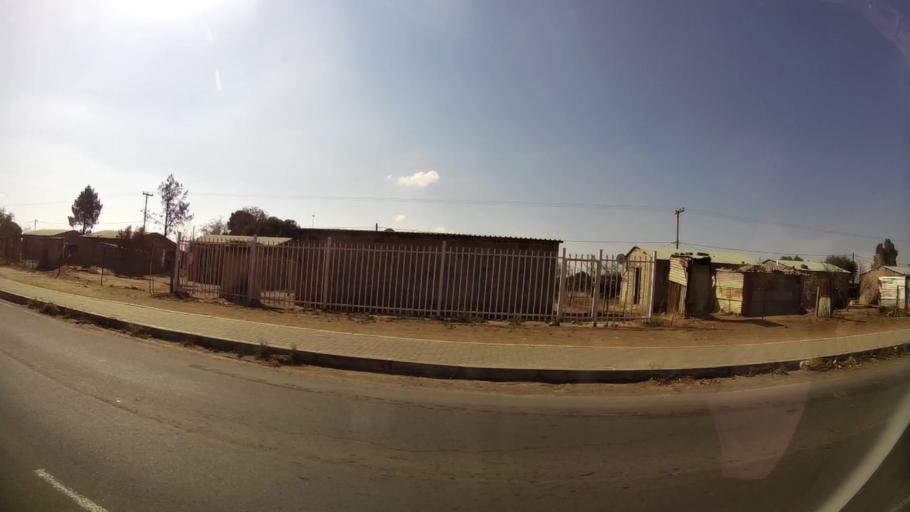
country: ZA
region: Orange Free State
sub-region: Mangaung Metropolitan Municipality
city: Bloemfontein
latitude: -29.1565
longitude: 26.2748
